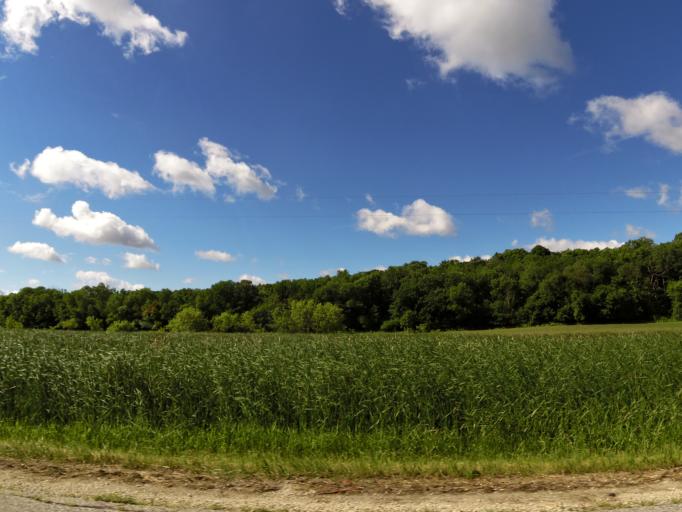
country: US
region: Minnesota
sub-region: Olmsted County
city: Rochester
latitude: 44.0110
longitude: -92.3843
